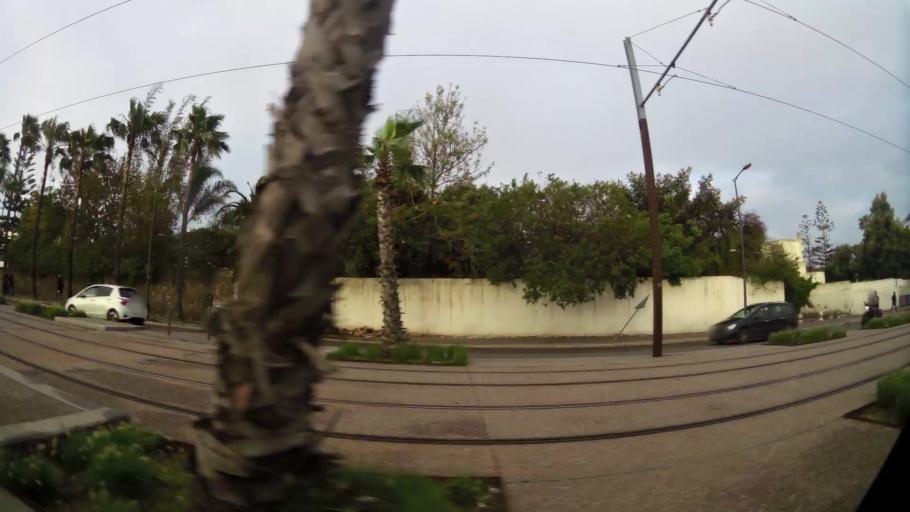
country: MA
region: Grand Casablanca
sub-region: Casablanca
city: Casablanca
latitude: 33.5784
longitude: -7.6740
